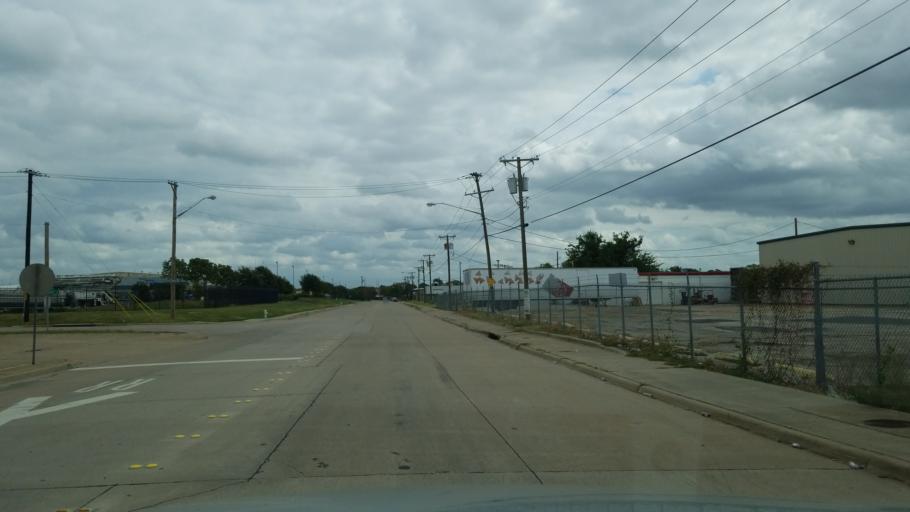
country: US
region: Texas
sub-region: Dallas County
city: Garland
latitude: 32.8866
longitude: -96.6741
